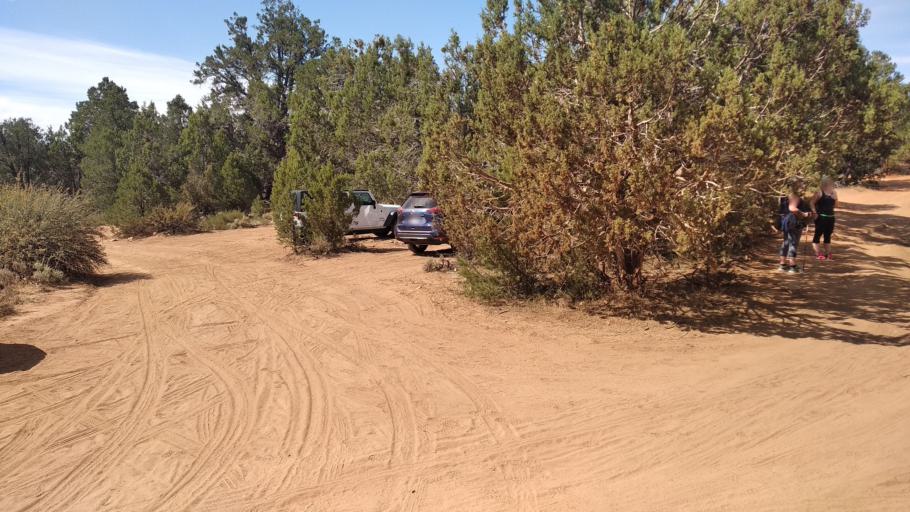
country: US
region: Utah
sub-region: Washington County
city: Hildale
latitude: 37.2970
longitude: -112.9001
